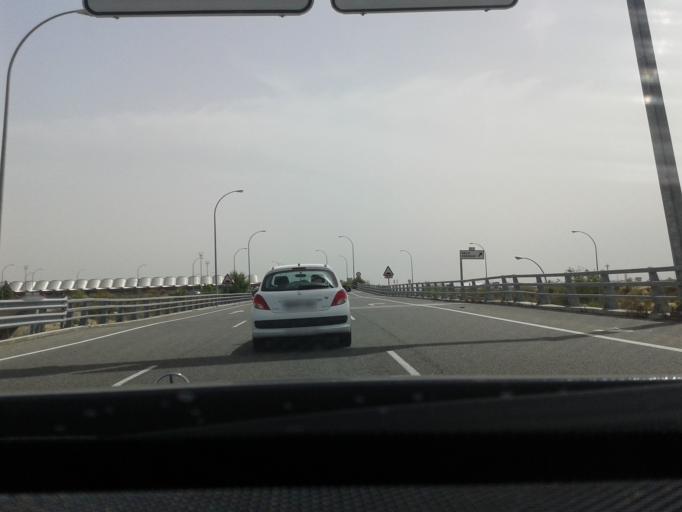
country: ES
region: Madrid
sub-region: Provincia de Madrid
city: Barajas de Madrid
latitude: 40.4865
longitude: -3.5972
